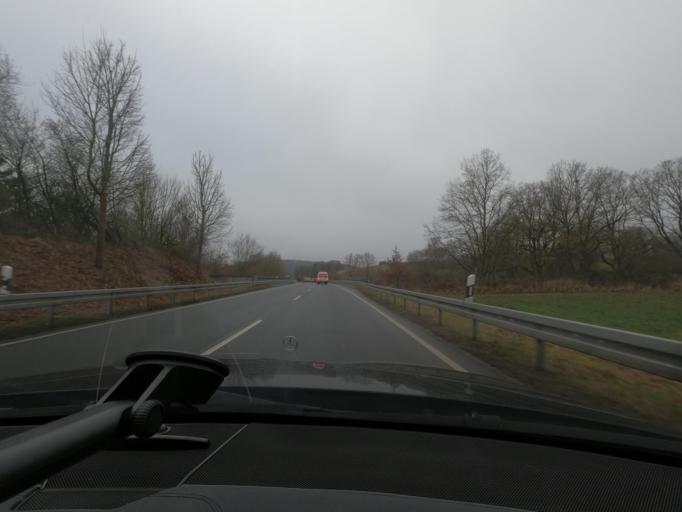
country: DE
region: Hesse
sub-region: Regierungsbezirk Kassel
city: Bad Arolsen
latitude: 51.3927
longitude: 9.0043
